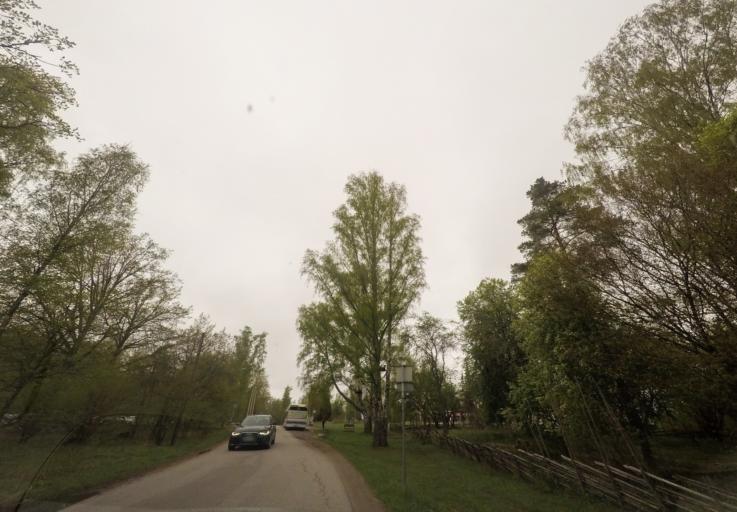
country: SE
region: Vaestmanland
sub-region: Vasteras
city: Vasteras
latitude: 59.5755
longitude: 16.6117
